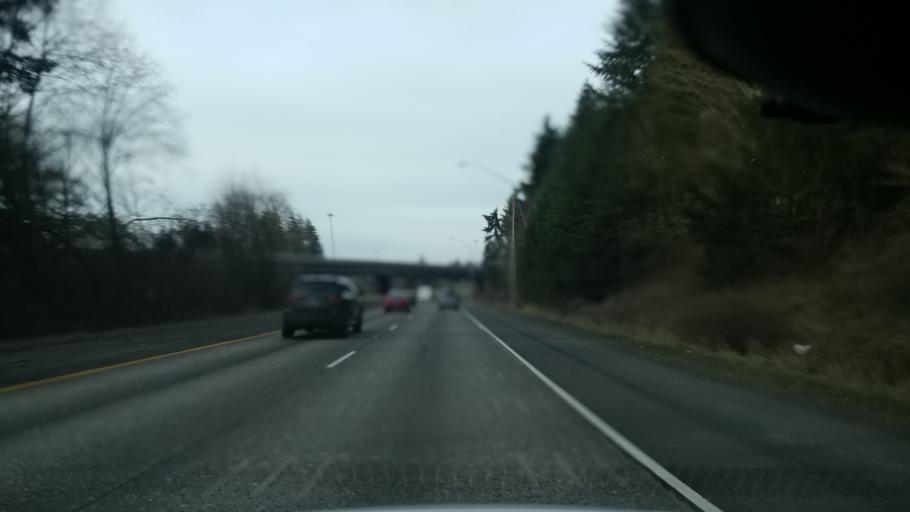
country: US
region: Washington
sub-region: Clark County
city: Salmon Creek
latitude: 45.7184
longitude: -122.6496
